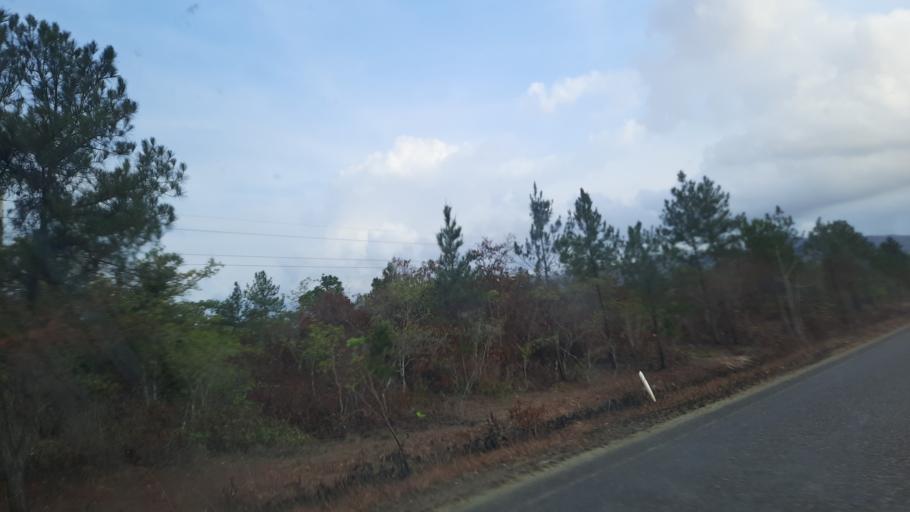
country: BZ
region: Stann Creek
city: Placencia
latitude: 16.6851
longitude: -88.4383
